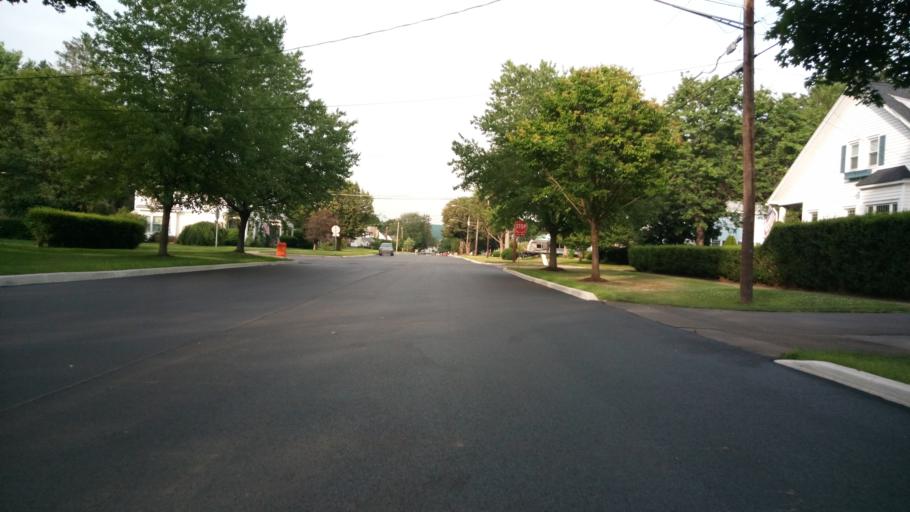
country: US
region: New York
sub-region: Chemung County
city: West Elmira
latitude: 42.0861
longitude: -76.8279
